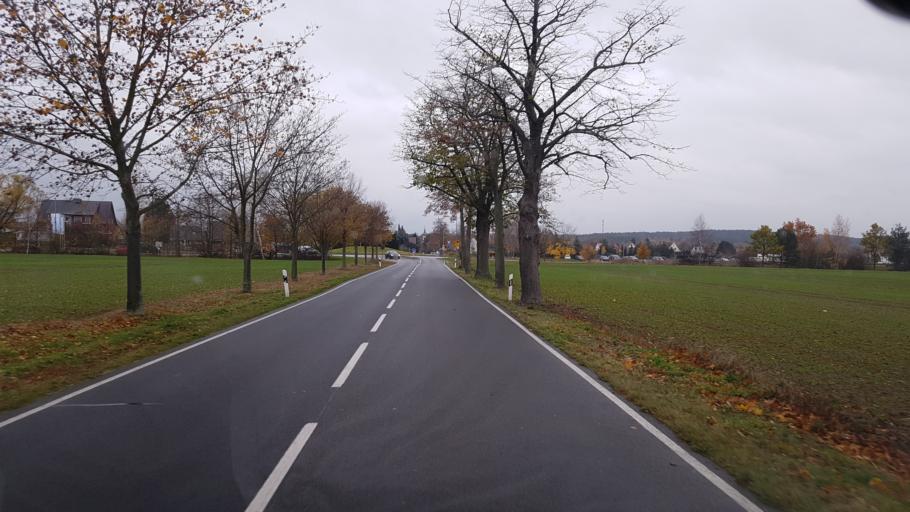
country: DE
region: Brandenburg
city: Ortrand
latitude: 51.3845
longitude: 13.7614
